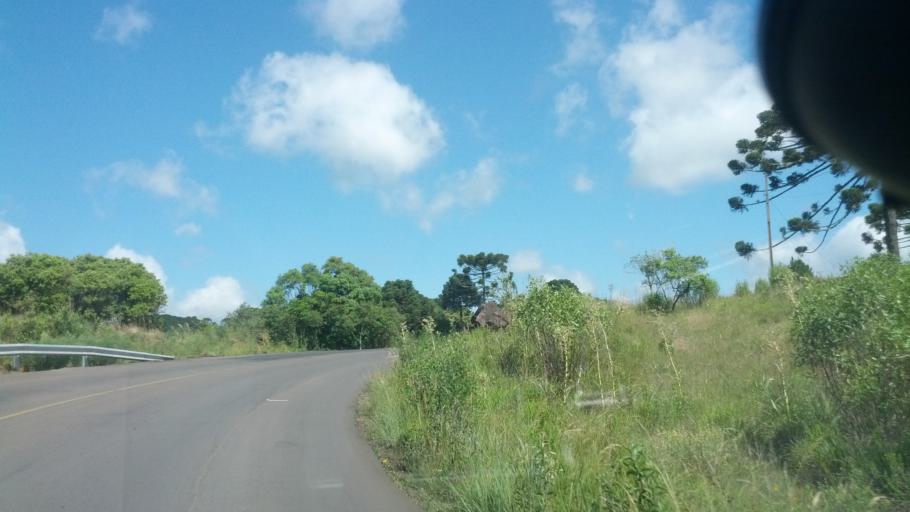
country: BR
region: Santa Catarina
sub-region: Lages
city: Lages
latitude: -27.9334
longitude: -50.5281
